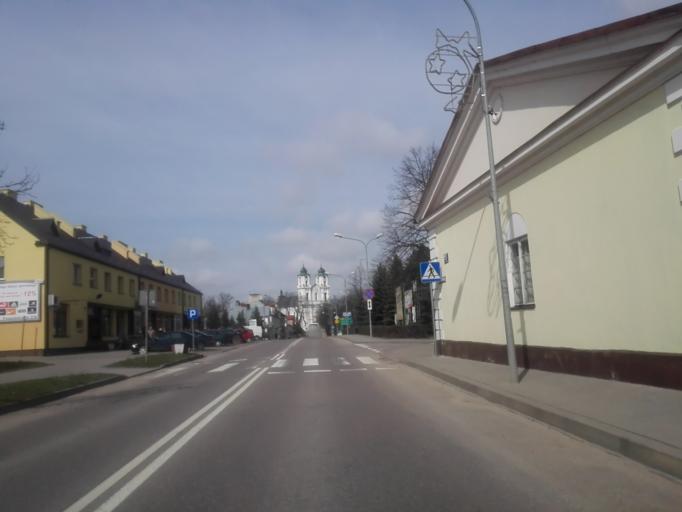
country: PL
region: Podlasie
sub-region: Powiat sejnenski
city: Sejny
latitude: 54.1063
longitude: 23.3497
